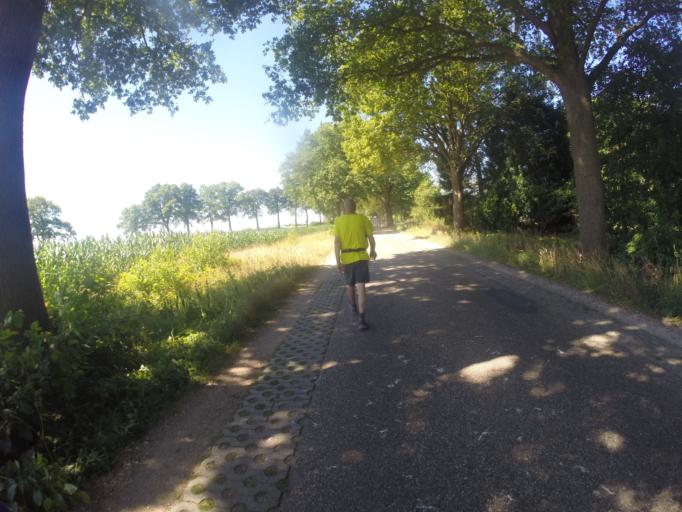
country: NL
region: Gelderland
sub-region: Gemeente Lochem
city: Lochem
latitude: 52.1352
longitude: 6.4124
